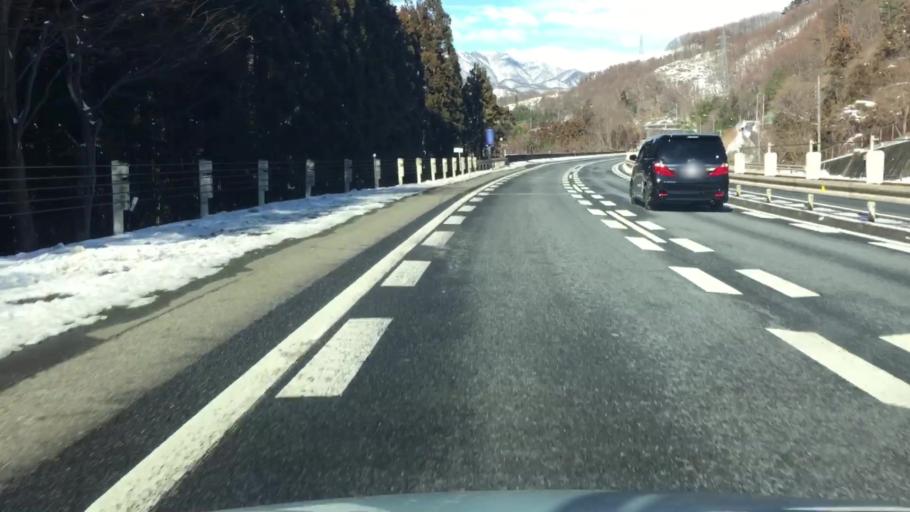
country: JP
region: Gunma
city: Numata
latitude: 36.6933
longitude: 138.9934
